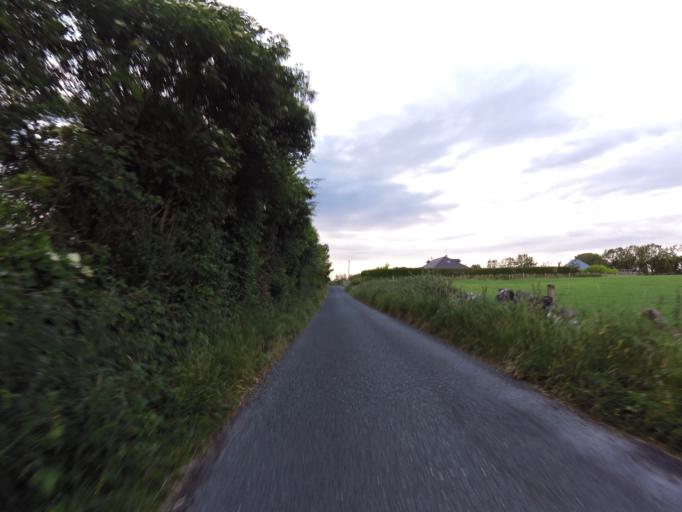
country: IE
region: Connaught
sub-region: County Galway
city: Athenry
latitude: 53.2902
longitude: -8.7161
